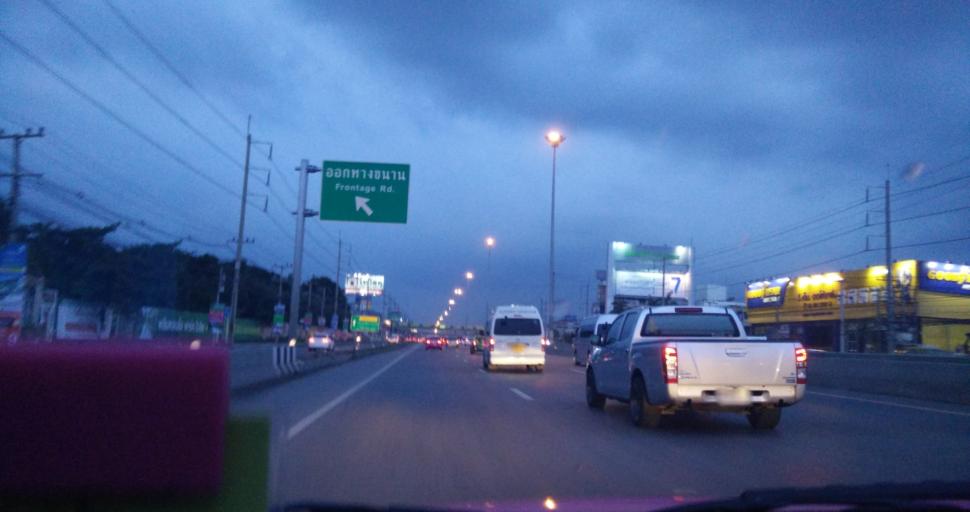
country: TH
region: Pathum Thani
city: Khlong Luang
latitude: 14.0121
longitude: 100.6152
